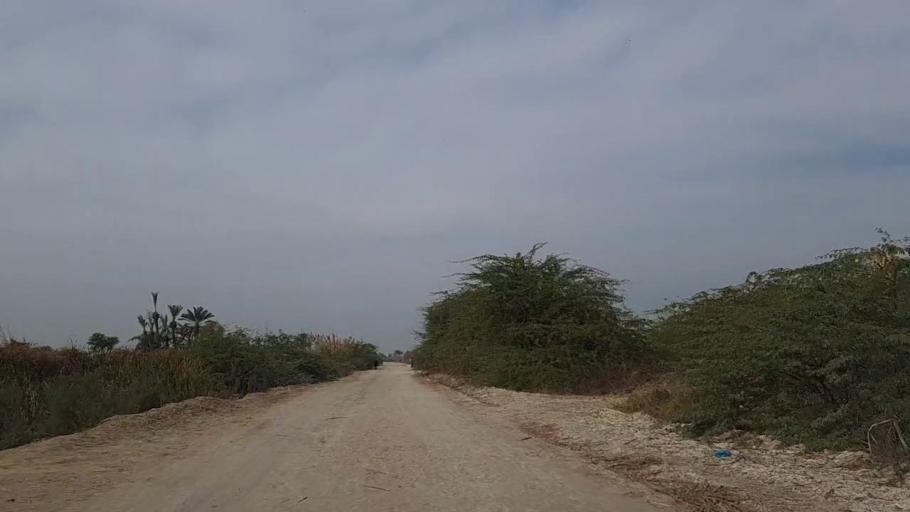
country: PK
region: Sindh
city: Daur
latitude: 26.4034
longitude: 68.4388
